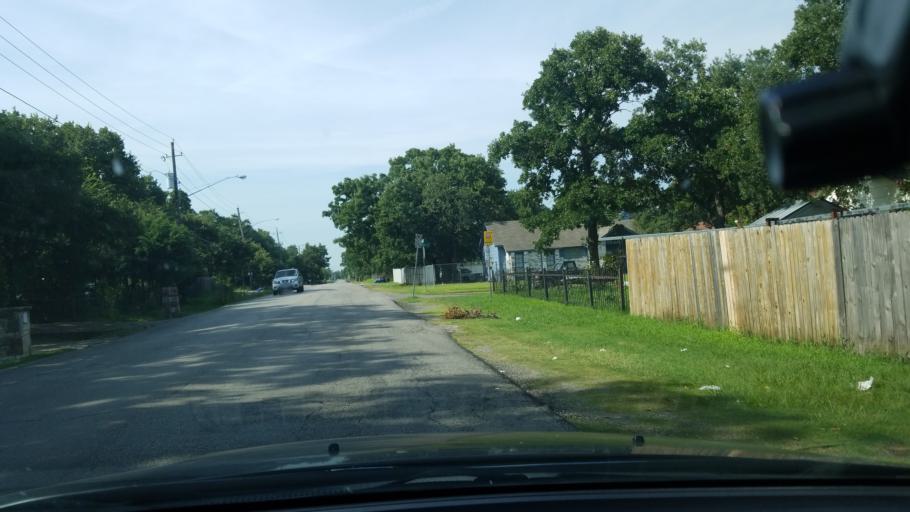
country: US
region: Texas
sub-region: Dallas County
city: Balch Springs
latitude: 32.7304
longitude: -96.6392
